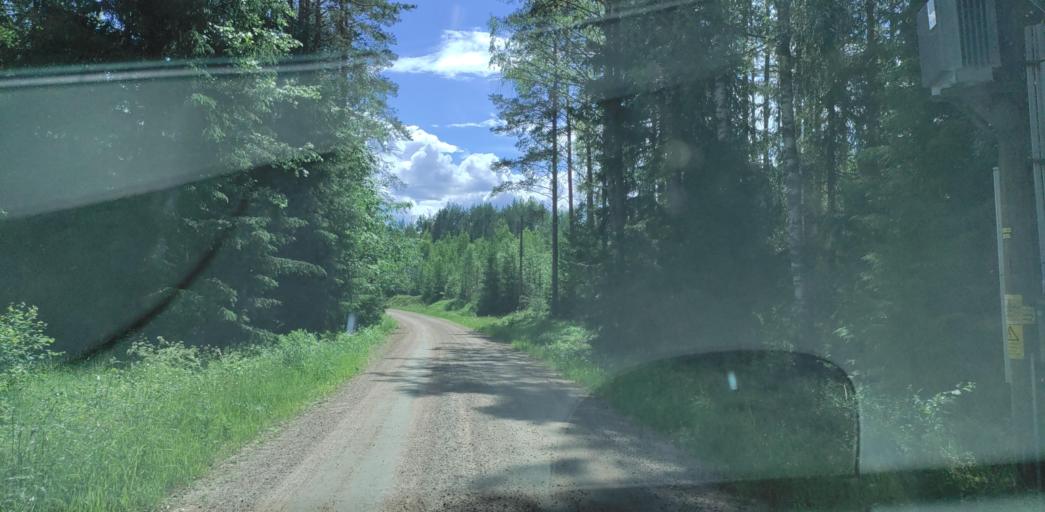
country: SE
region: Vaermland
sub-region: Munkfors Kommun
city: Munkfors
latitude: 59.9677
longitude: 13.5222
